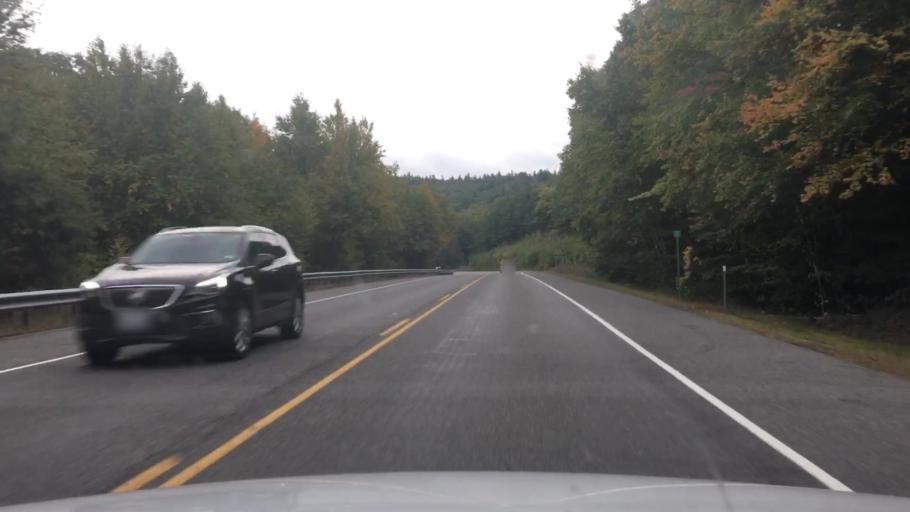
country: US
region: New Hampshire
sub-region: Carroll County
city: Wolfeboro
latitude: 43.5225
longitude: -71.2736
